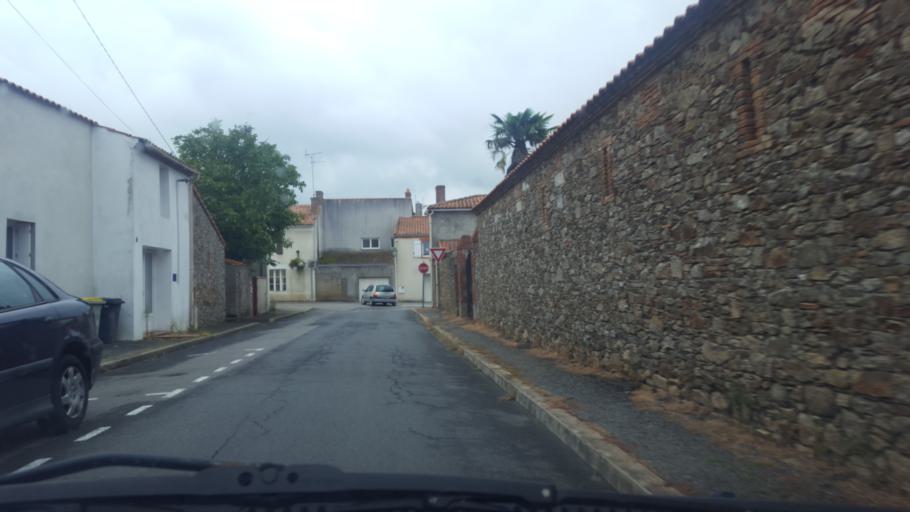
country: FR
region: Pays de la Loire
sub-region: Departement de la Loire-Atlantique
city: Saint-Lumine-de-Coutais
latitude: 47.0557
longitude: -1.7259
